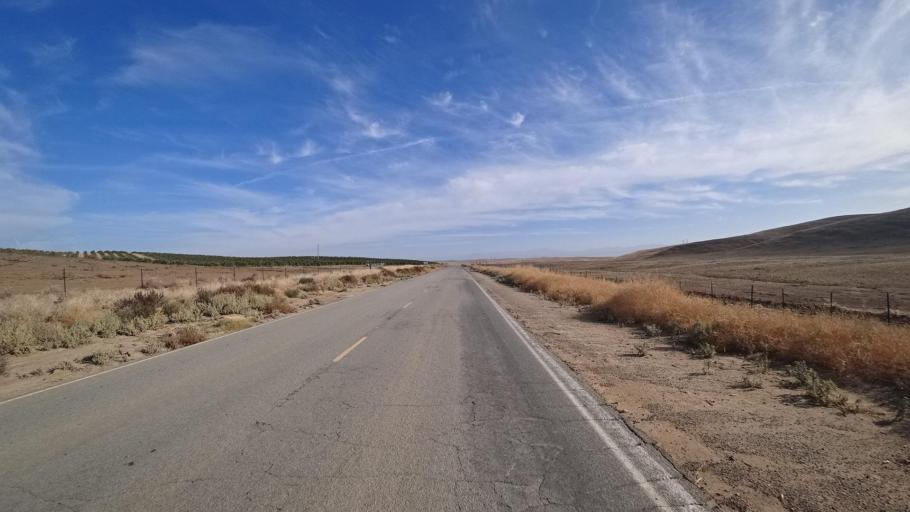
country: US
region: California
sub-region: Kern County
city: McFarland
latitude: 35.6160
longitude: -119.0505
